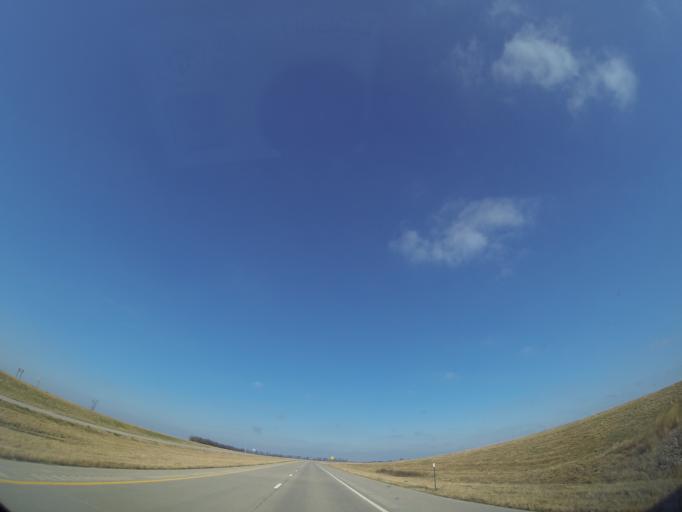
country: US
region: Kansas
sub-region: McPherson County
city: Inman
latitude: 38.2319
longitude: -97.7841
